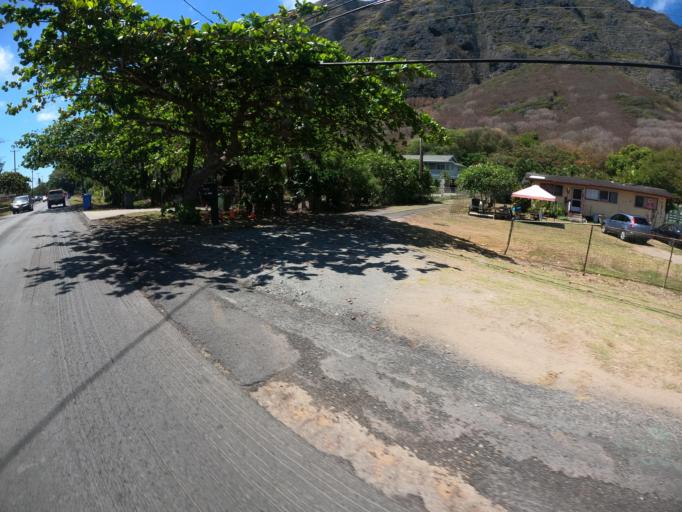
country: US
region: Hawaii
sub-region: Honolulu County
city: Waimanalo Beach
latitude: 21.3259
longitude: -157.6848
